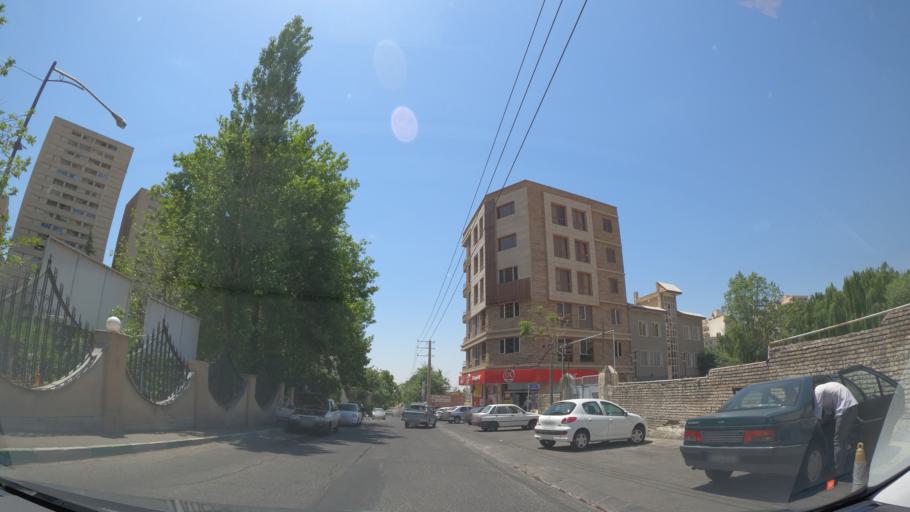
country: IR
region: Tehran
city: Tajrish
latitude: 35.7850
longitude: 51.3887
